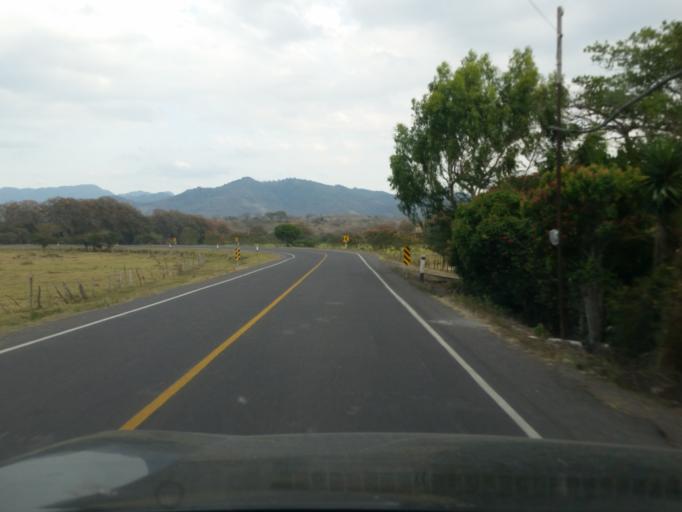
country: NI
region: Jinotega
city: Jinotega
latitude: 13.1415
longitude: -86.0472
